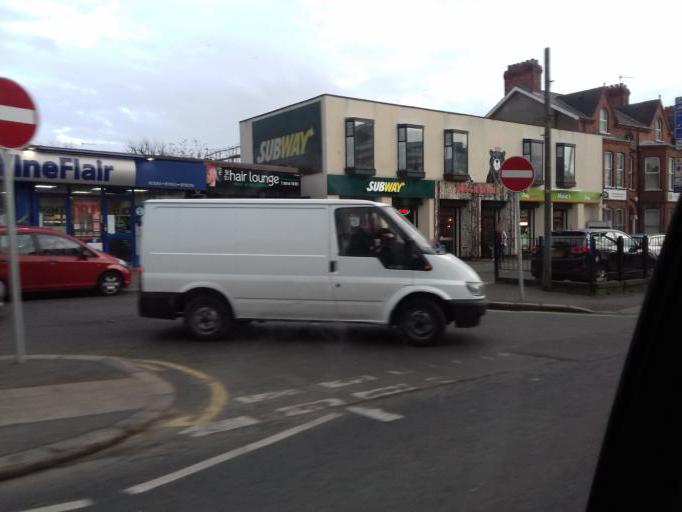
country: GB
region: Northern Ireland
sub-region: City of Belfast
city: Belfast
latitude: 54.6258
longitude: -5.9378
